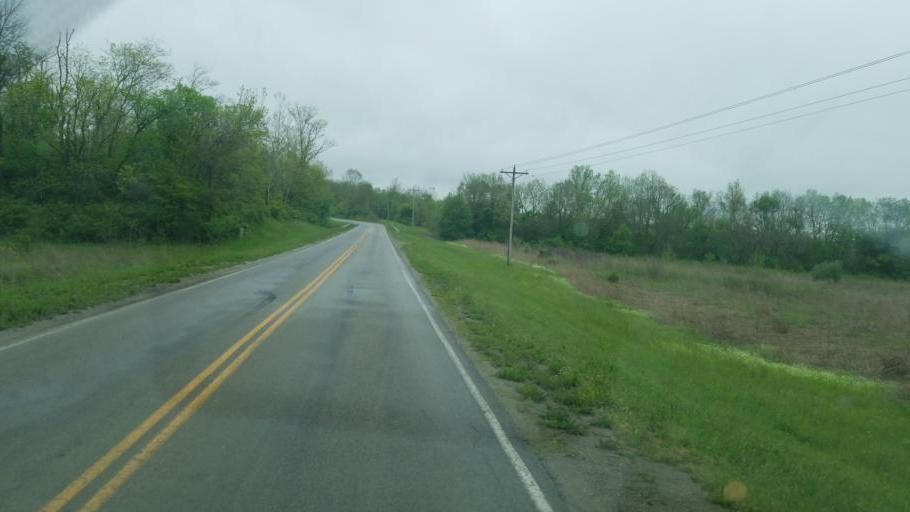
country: US
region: Ohio
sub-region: Highland County
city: Greenfield
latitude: 39.3352
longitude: -83.4642
